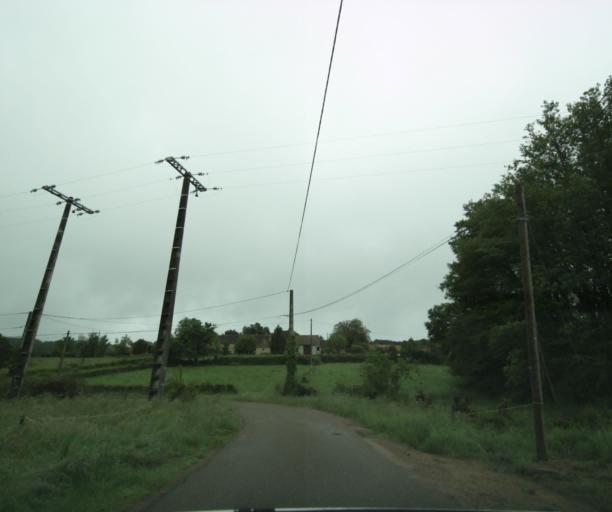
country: FR
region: Bourgogne
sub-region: Departement de Saone-et-Loire
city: Charolles
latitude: 46.4558
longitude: 4.3988
